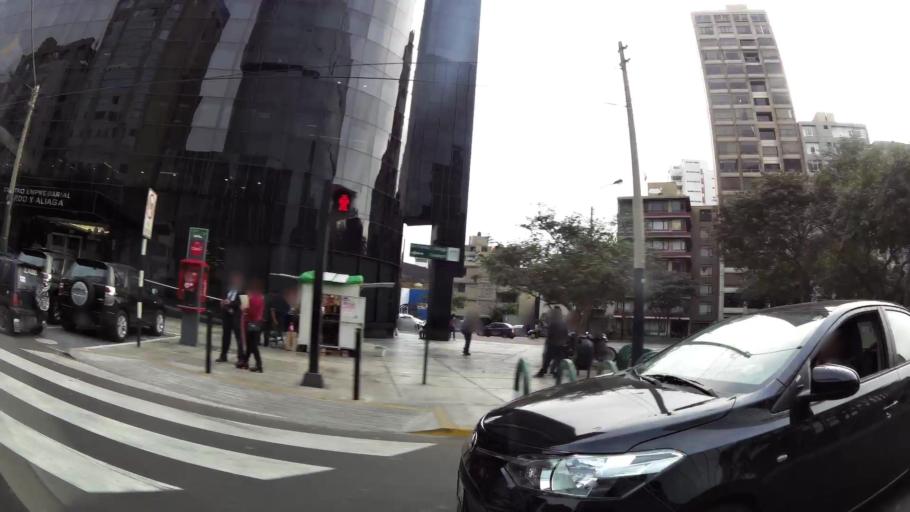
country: PE
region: Lima
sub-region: Lima
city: San Isidro
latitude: -12.1062
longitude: -77.0389
